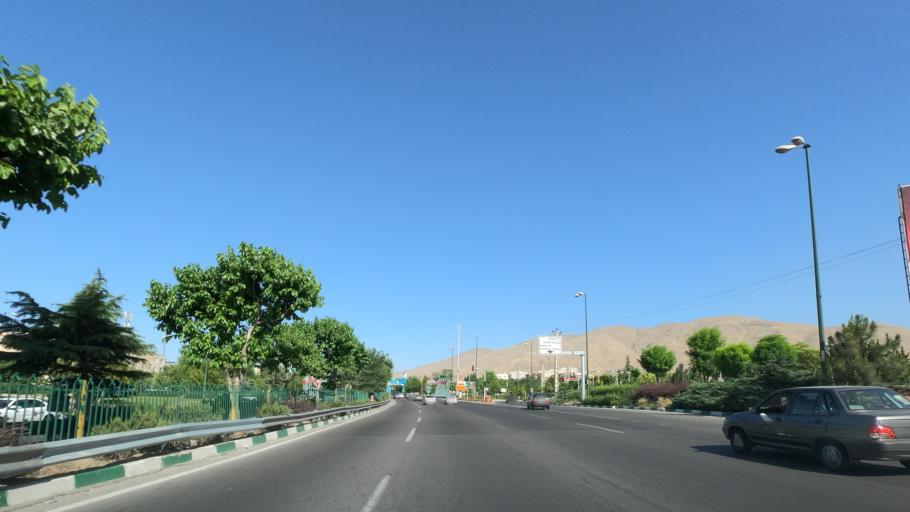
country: IR
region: Tehran
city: Shahr-e Qods
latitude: 35.7569
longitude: 51.2670
